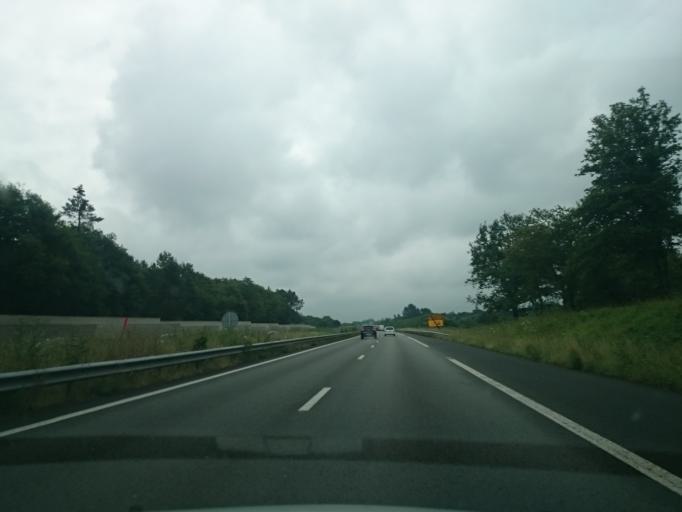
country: FR
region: Pays de la Loire
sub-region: Departement de la Loire-Atlantique
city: Sautron
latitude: 47.2576
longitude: -1.6920
